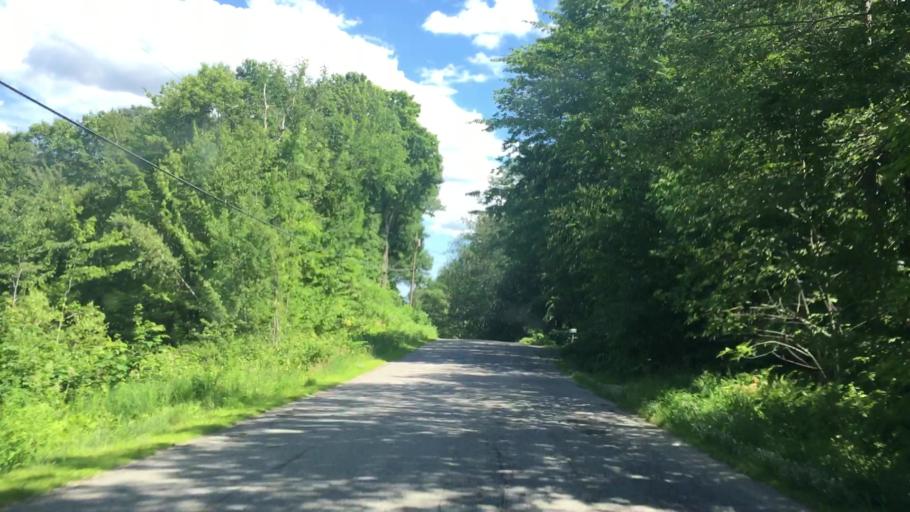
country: US
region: Maine
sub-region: Franklin County
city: Chesterville
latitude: 44.5651
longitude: -70.1424
